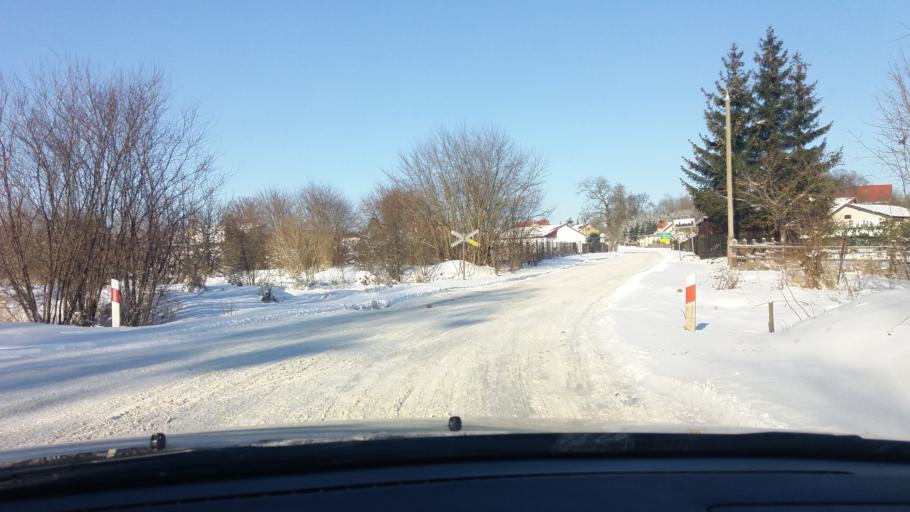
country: PL
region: Warmian-Masurian Voivodeship
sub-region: Powiat nidzicki
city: Nidzica
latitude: 53.3717
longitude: 20.6050
